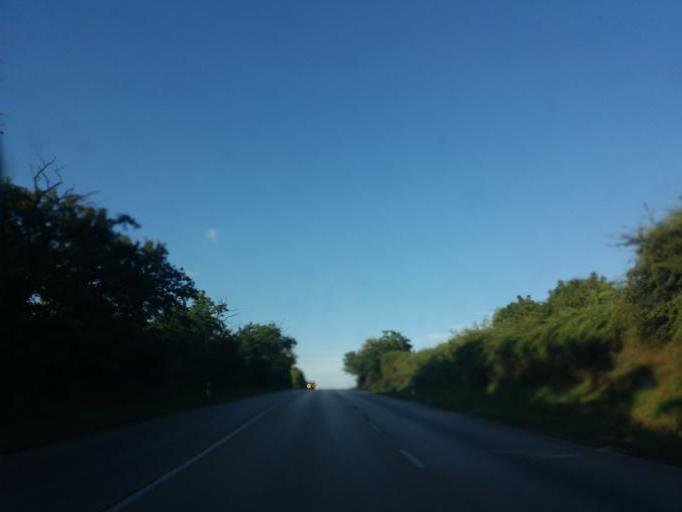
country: HU
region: Fejer
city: Baracska
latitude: 47.2967
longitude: 18.7647
